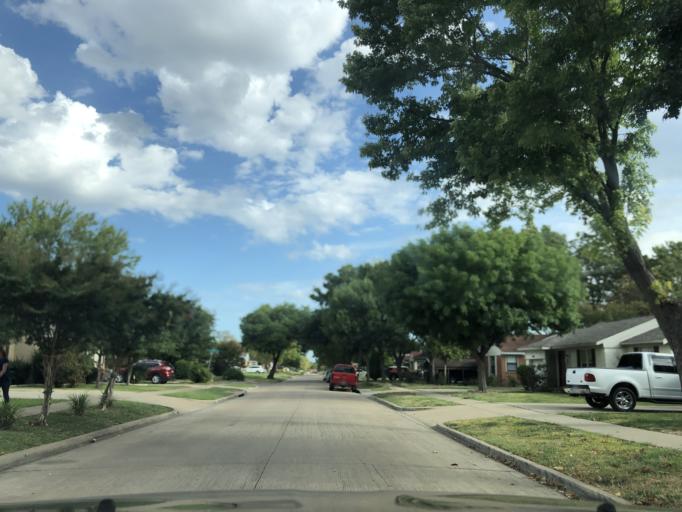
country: US
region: Texas
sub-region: Dallas County
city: Garland
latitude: 32.8800
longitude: -96.6616
